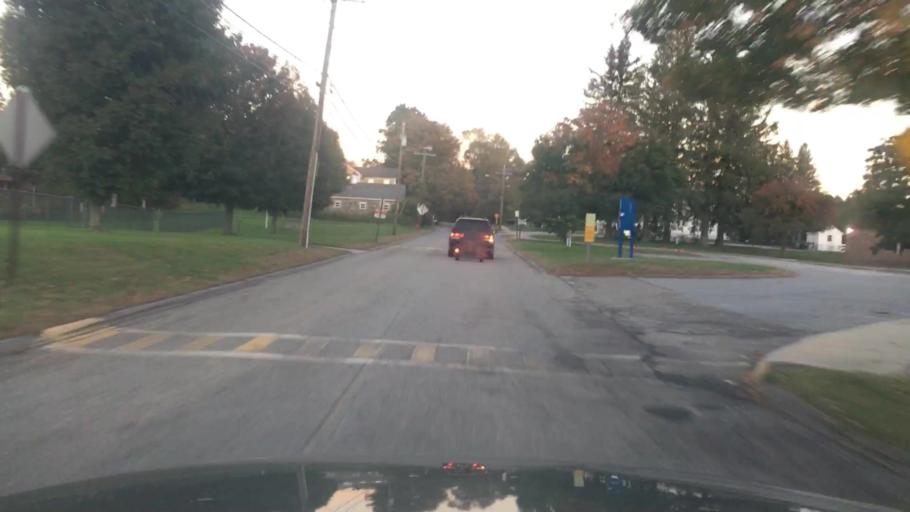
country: US
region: Massachusetts
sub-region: Worcester County
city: Charlton
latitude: 42.1326
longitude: -71.9716
